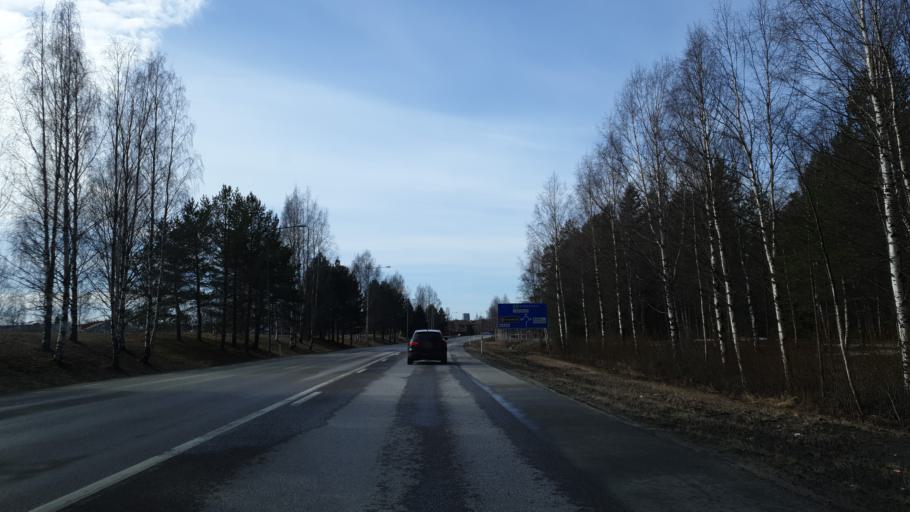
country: SE
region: Vaesterbotten
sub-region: Umea Kommun
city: Umea
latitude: 63.8396
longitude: 20.2743
